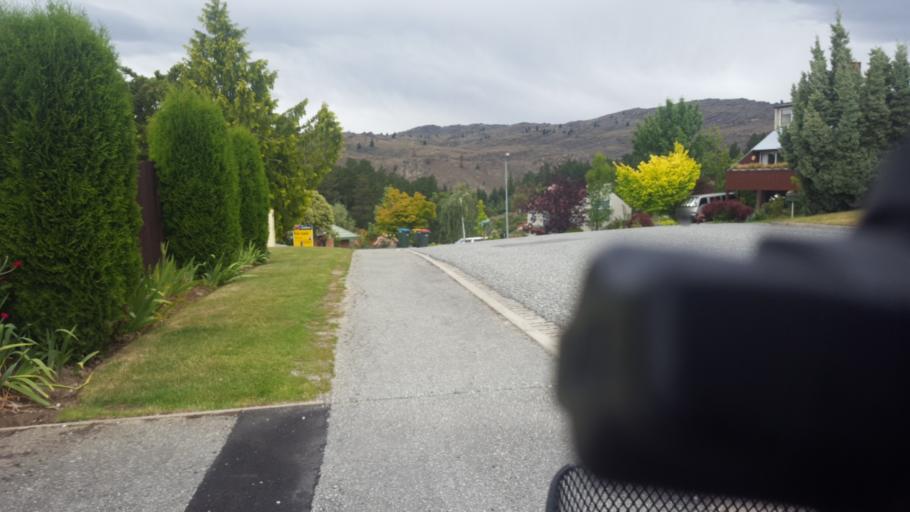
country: NZ
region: Otago
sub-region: Queenstown-Lakes District
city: Wanaka
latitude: -45.2611
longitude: 169.3820
